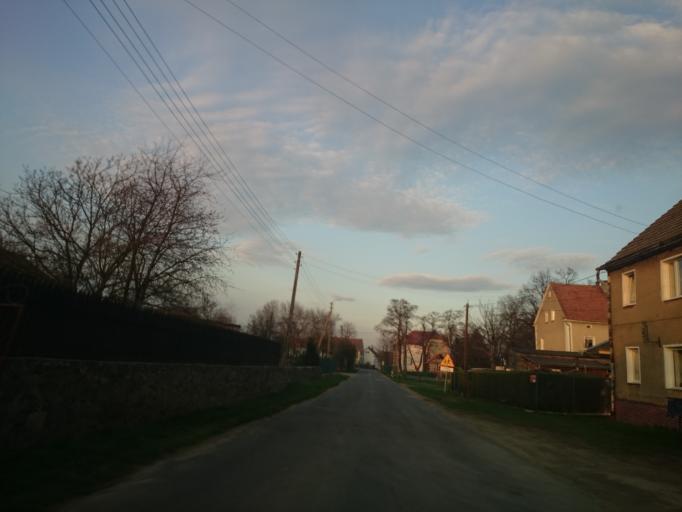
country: PL
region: Lower Silesian Voivodeship
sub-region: Powiat zabkowicki
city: Zabkowice Slaskie
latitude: 50.5532
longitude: 16.7870
